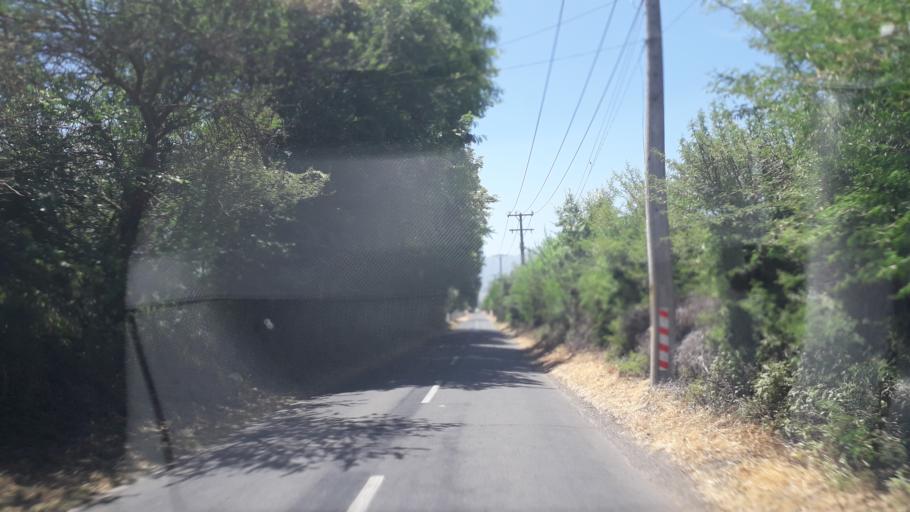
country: CL
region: Valparaiso
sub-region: Provincia de Quillota
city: Quillota
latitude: -32.9288
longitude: -71.2541
